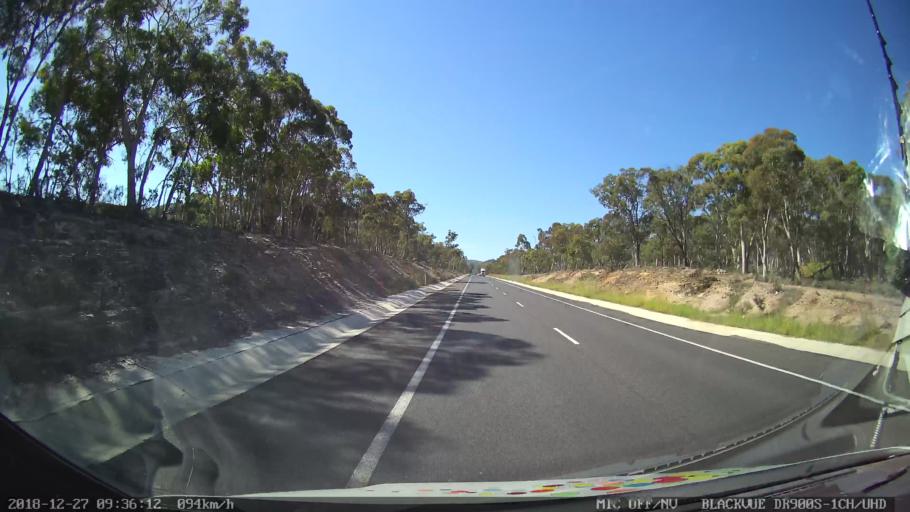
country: AU
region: New South Wales
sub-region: Lithgow
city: Portland
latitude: -33.2490
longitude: 150.0338
